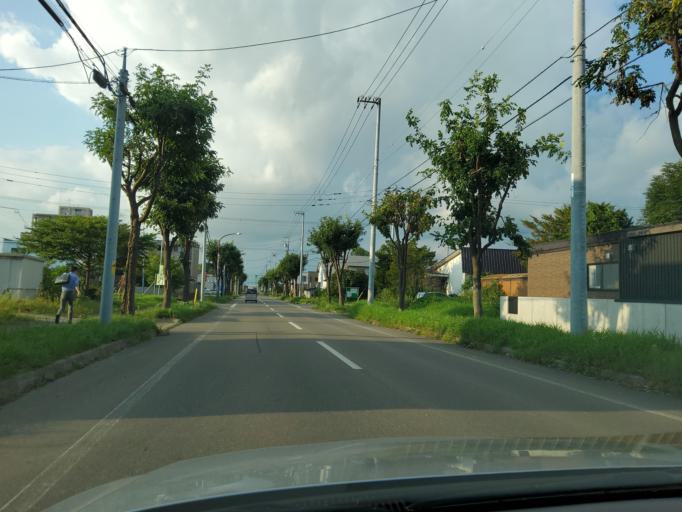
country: JP
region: Hokkaido
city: Obihiro
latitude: 42.9173
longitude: 143.1851
